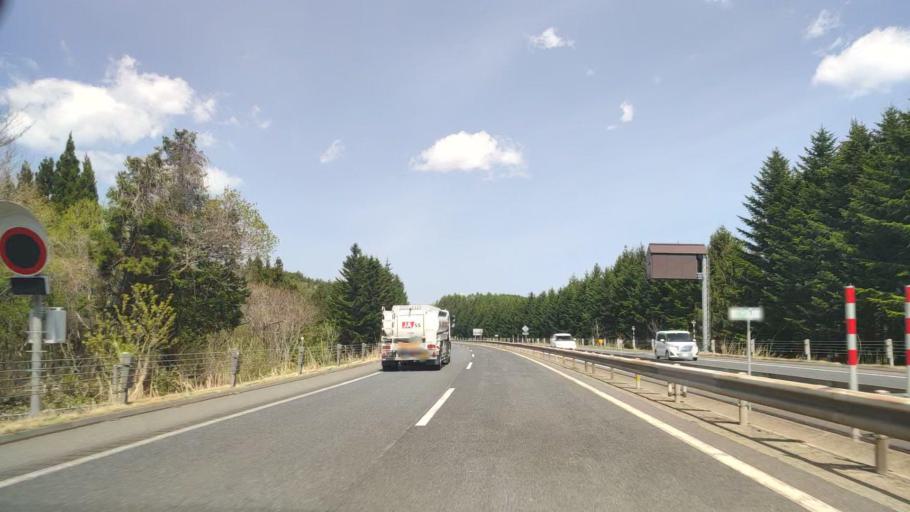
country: JP
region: Aomori
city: Hachinohe
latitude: 40.4118
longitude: 141.4437
